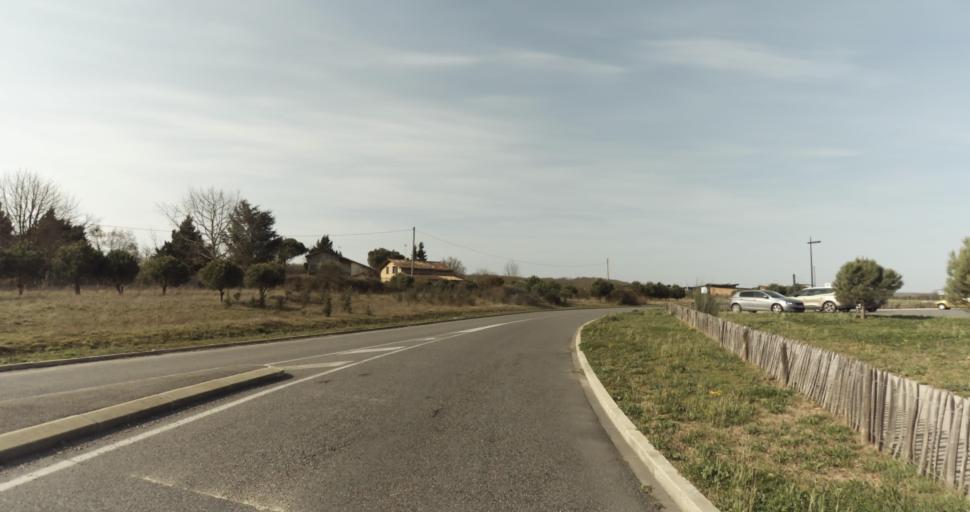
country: FR
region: Midi-Pyrenees
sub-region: Departement du Tarn
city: Saint-Sulpice-la-Pointe
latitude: 43.7529
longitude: 1.6591
